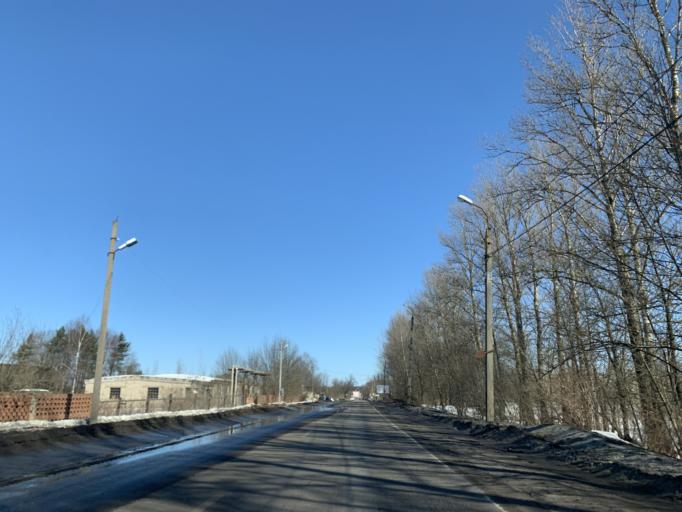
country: RU
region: Jaroslavl
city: Konstantinovskiy
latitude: 57.8391
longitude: 39.5690
